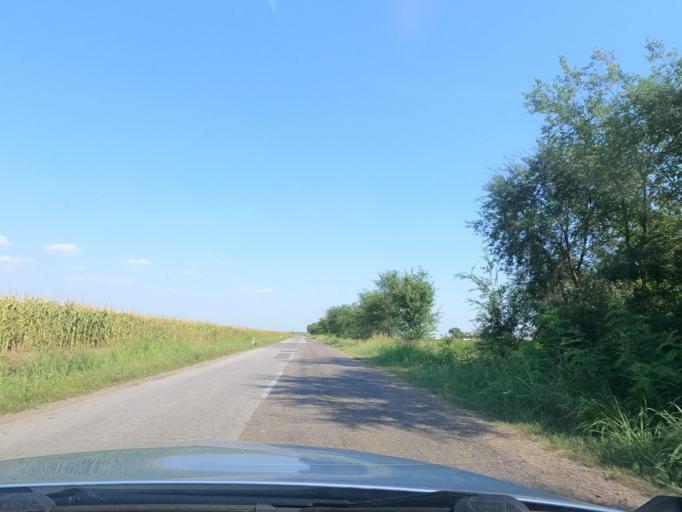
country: RS
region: Autonomna Pokrajina Vojvodina
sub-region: Juznobacki Okrug
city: Becej
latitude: 45.6524
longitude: 19.9696
